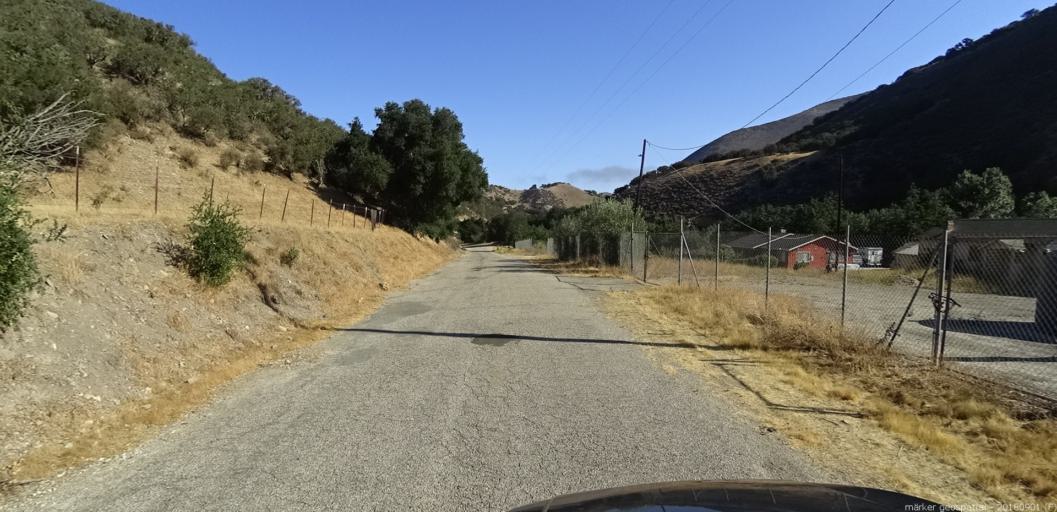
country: US
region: California
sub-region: Monterey County
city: Greenfield
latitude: 36.2116
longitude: -121.2798
